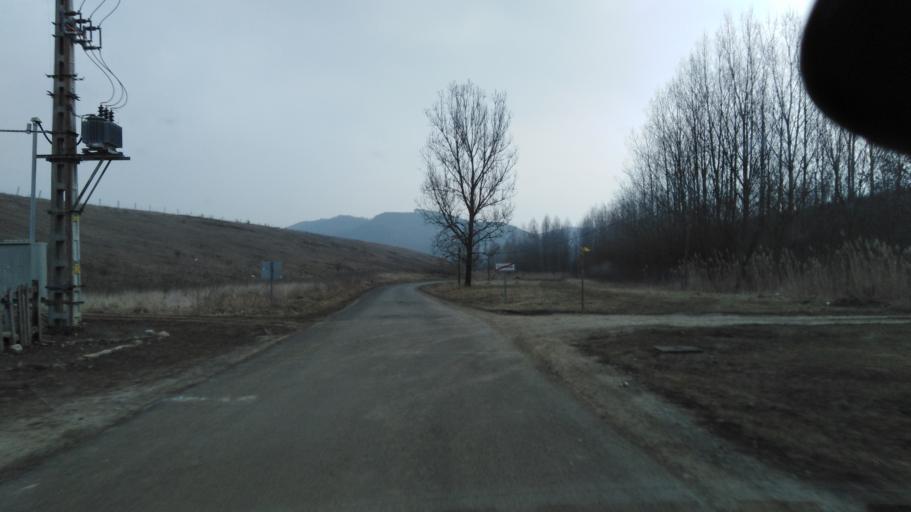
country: HU
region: Nograd
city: Tar
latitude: 48.0301
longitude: 19.7001
